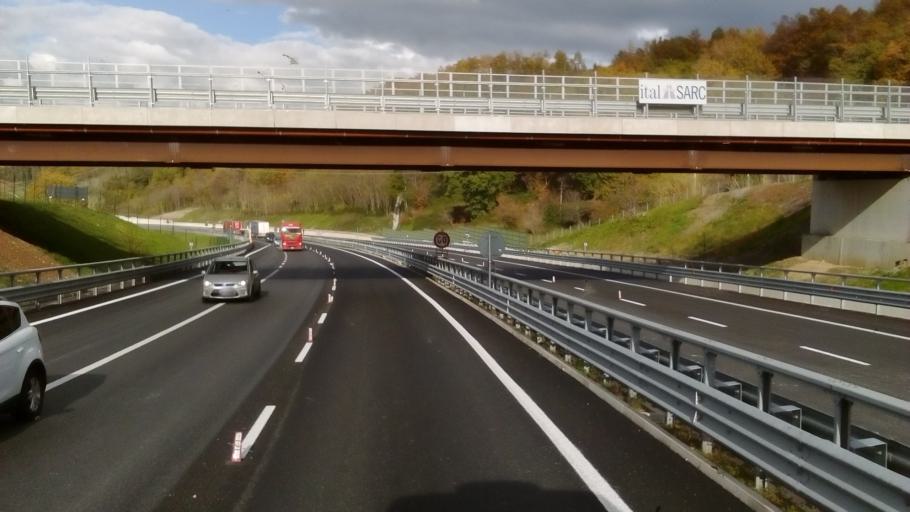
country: IT
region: Calabria
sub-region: Provincia di Cosenza
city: Laino Castello-Nuovo Centro
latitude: 39.9175
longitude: 15.9669
